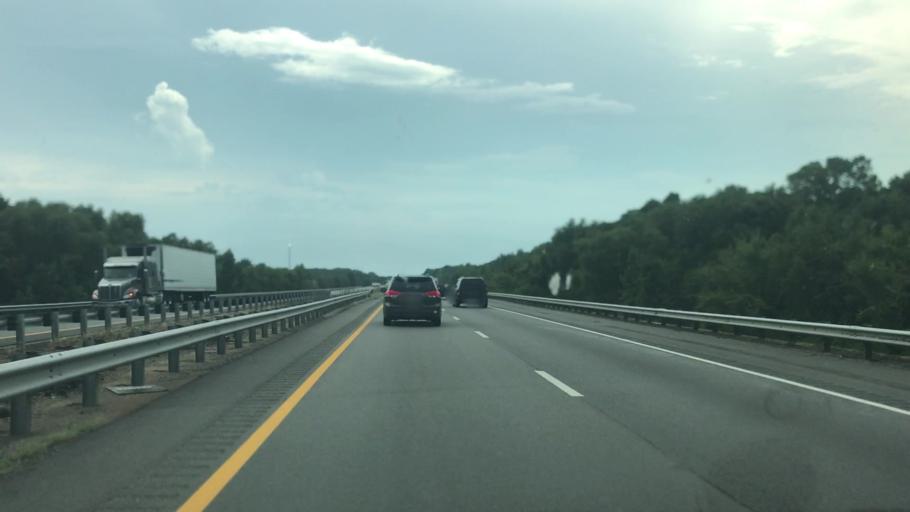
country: US
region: Arkansas
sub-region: Monroe County
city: Brinkley
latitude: 34.8851
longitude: -91.2598
